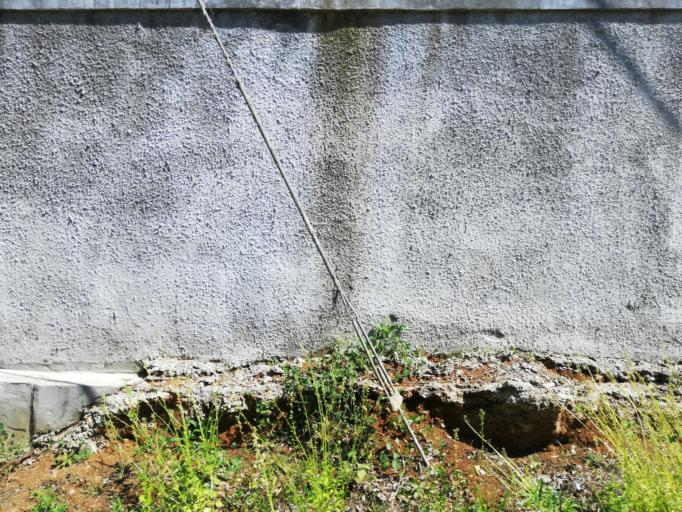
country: MU
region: Plaines Wilhems
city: Ebene
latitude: -20.2384
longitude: 57.4916
